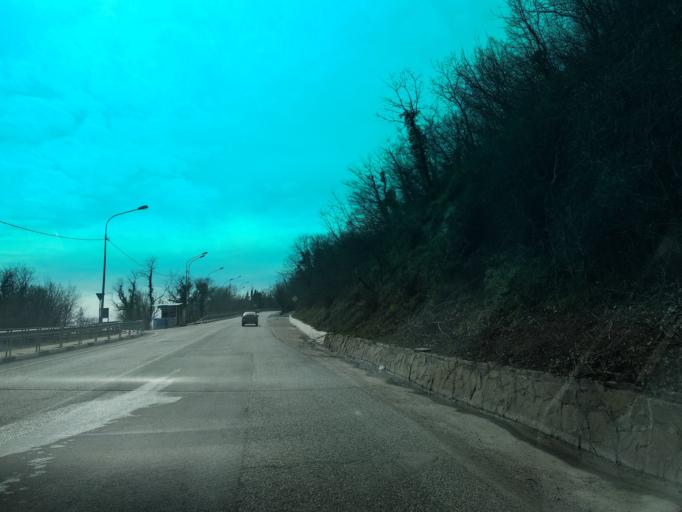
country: RU
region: Krasnodarskiy
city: Shepsi
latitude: 44.0424
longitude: 39.1491
